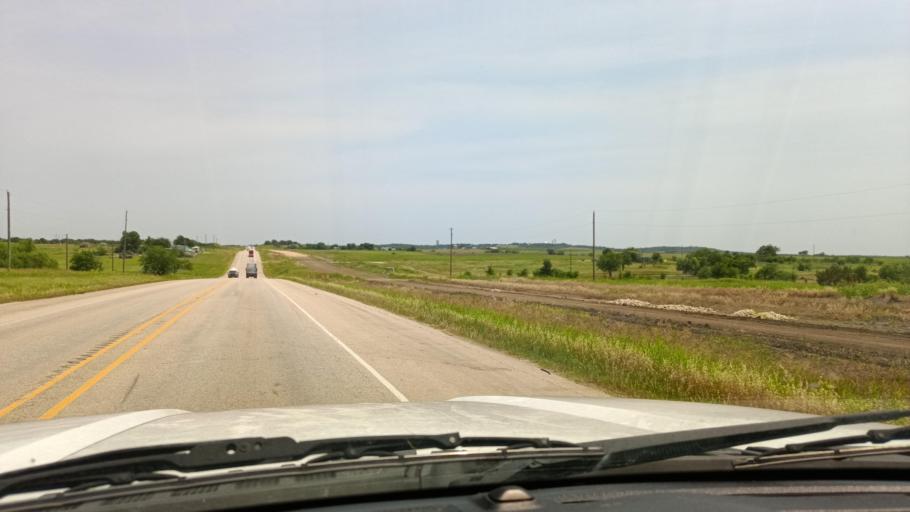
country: US
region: Texas
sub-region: Bell County
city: Rogers
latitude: 30.9798
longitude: -97.2746
